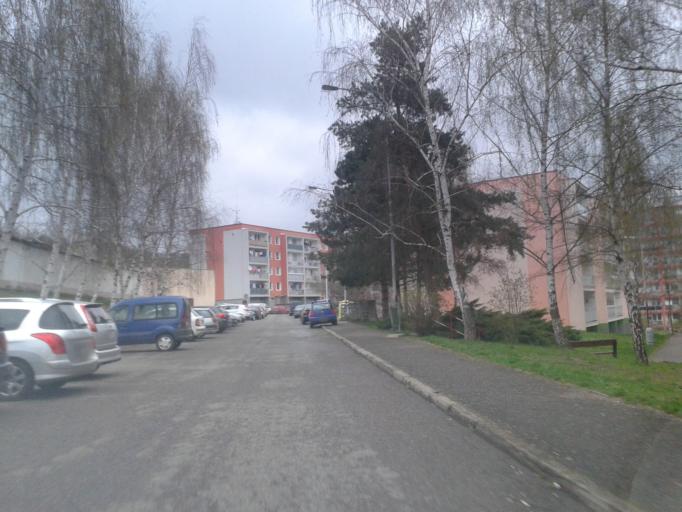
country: CZ
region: Central Bohemia
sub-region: Okres Beroun
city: Kraluv Dvur
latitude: 49.9453
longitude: 14.0256
